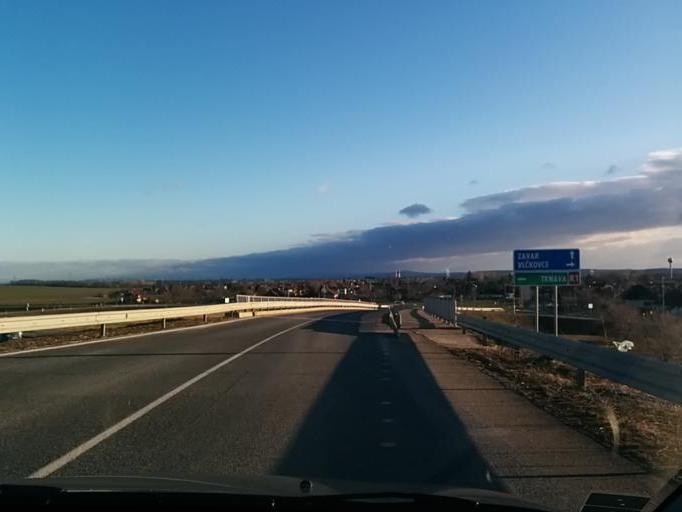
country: SK
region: Trnavsky
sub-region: Okres Trnava
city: Trnava
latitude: 48.3140
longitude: 17.6449
